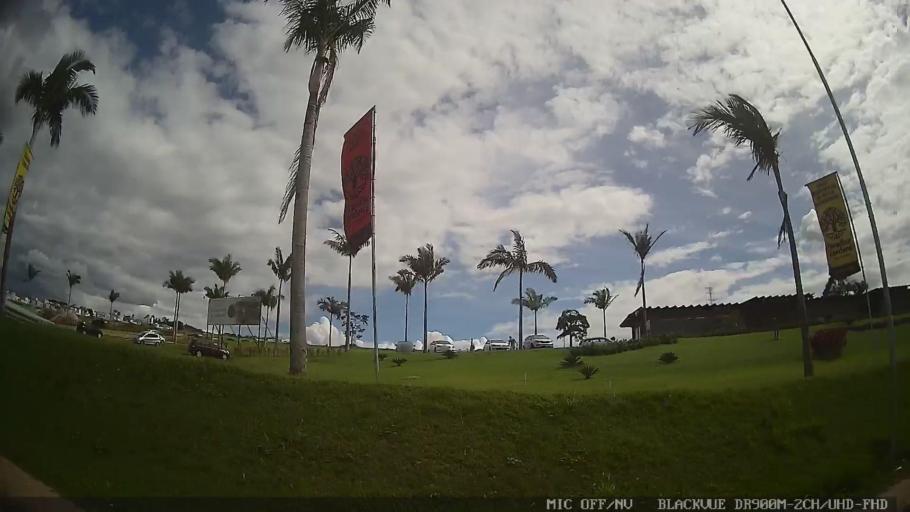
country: BR
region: Sao Paulo
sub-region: Mogi das Cruzes
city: Mogi das Cruzes
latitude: -23.5726
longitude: -46.1958
